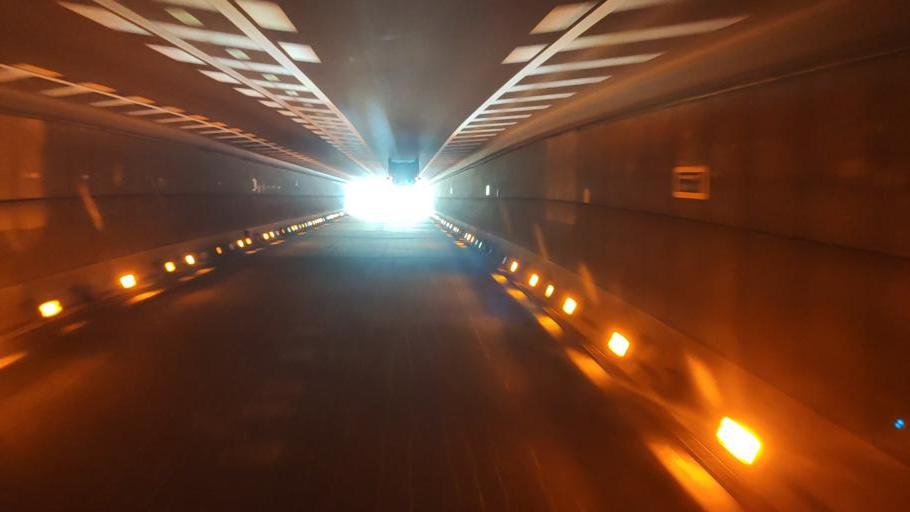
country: JP
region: Tokyo
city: Higashimurayama-shi
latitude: 35.7313
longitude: 139.4181
